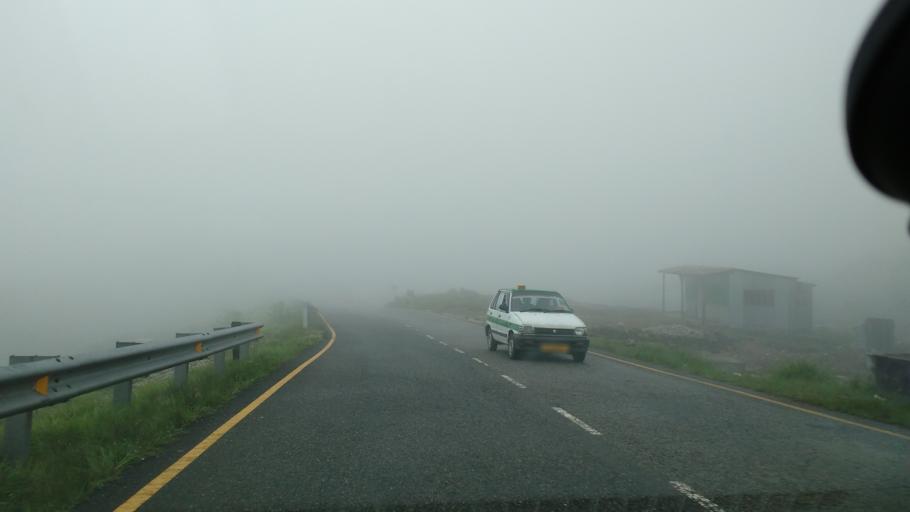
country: IN
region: Meghalaya
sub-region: East Khasi Hills
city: Cherrapunji
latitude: 25.3088
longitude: 91.7283
